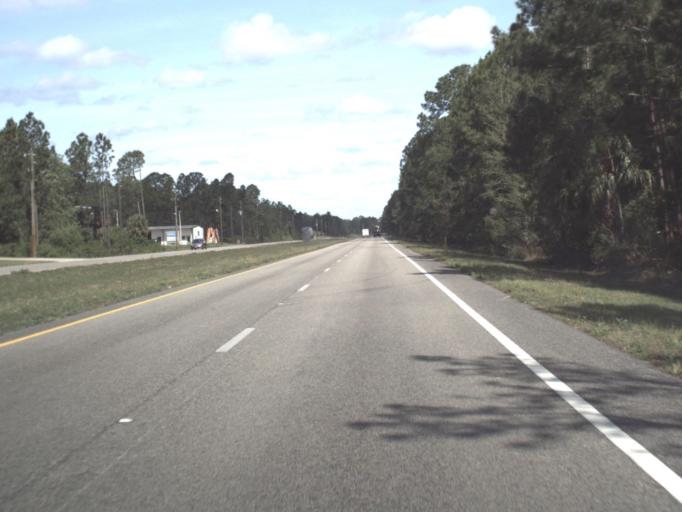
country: US
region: Florida
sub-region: Flagler County
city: Flagler Beach
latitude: 29.3768
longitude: -81.1811
